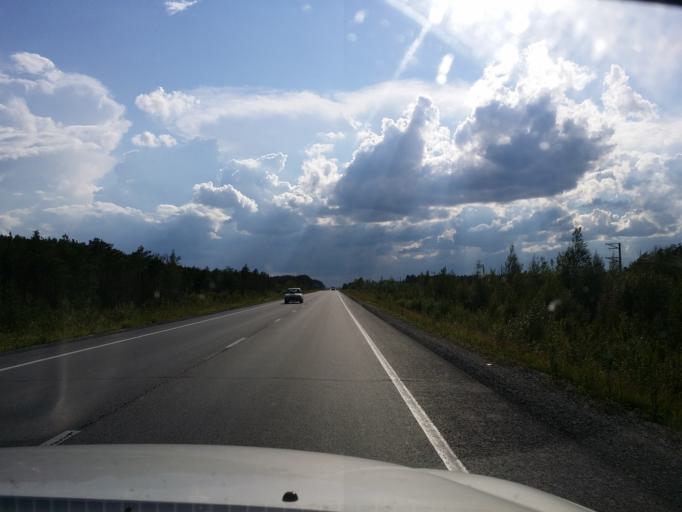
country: RU
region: Khanty-Mansiyskiy Avtonomnyy Okrug
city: Surgut
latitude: 61.4620
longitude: 74.0987
